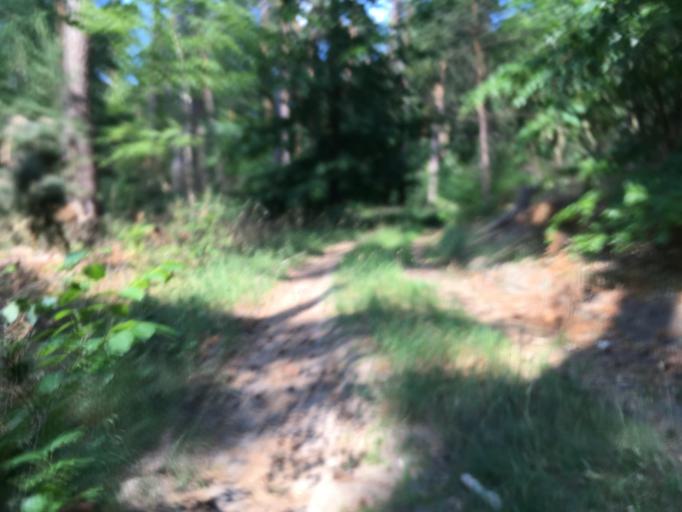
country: DE
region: Brandenburg
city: Marienwerder
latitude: 52.9231
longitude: 13.6561
